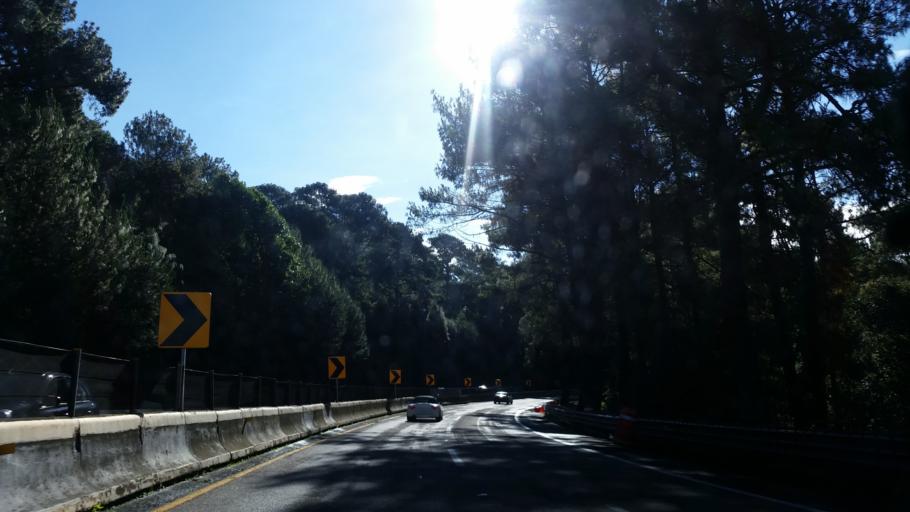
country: MX
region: Morelos
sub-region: Cuernavaca
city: Villa Santiago
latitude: 19.0279
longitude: -99.1822
